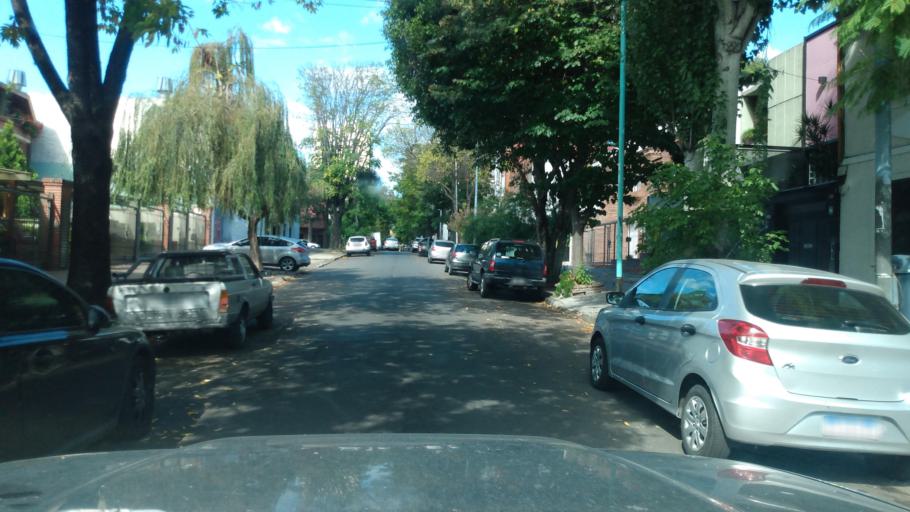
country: AR
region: Buenos Aires
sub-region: Partido de General San Martin
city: General San Martin
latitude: -34.5725
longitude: -58.4929
